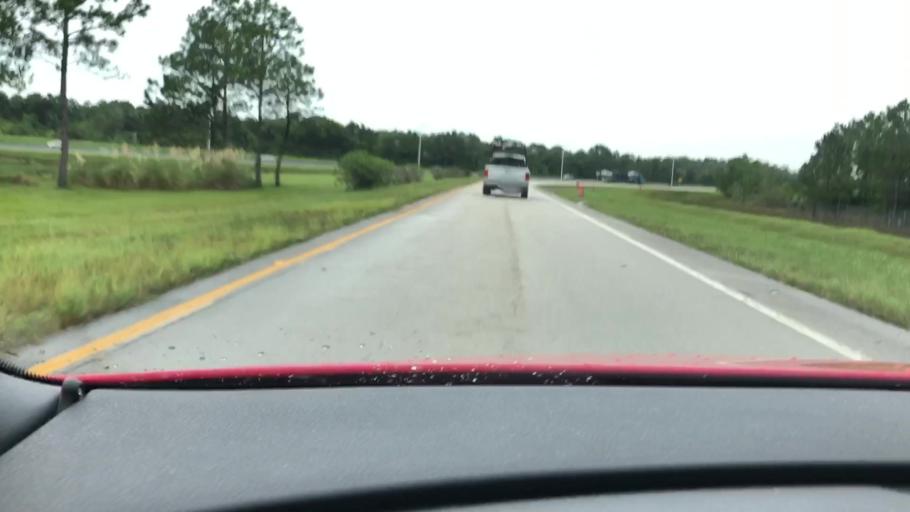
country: US
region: Florida
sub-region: Volusia County
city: Holly Hill
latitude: 29.2231
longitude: -81.1005
